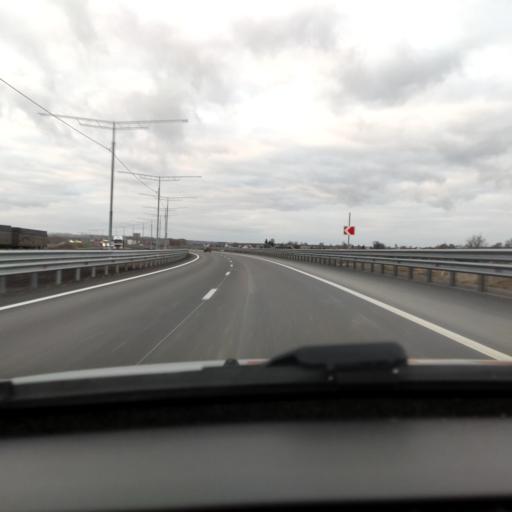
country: RU
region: Lipetsk
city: Khlevnoye
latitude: 52.0560
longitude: 39.1920
